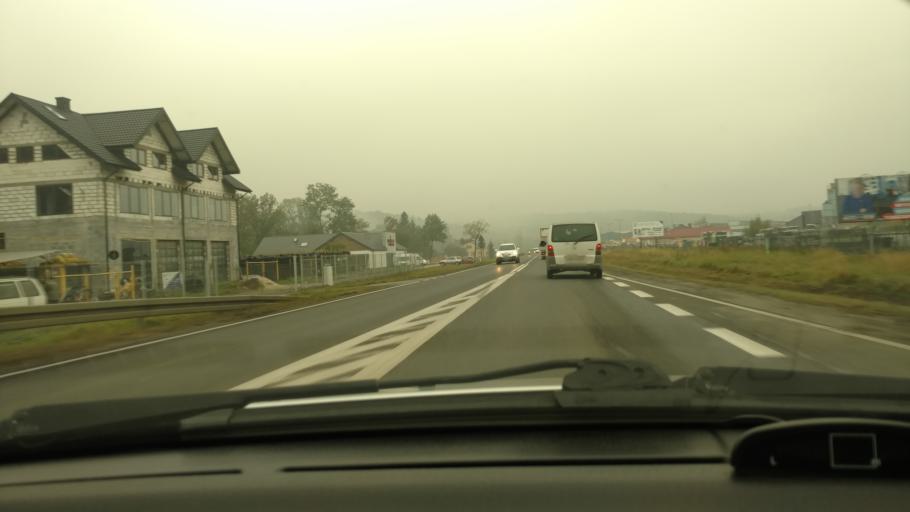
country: PL
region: Lesser Poland Voivodeship
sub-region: Powiat gorlicki
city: Kobylanka
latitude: 49.6829
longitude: 21.1903
